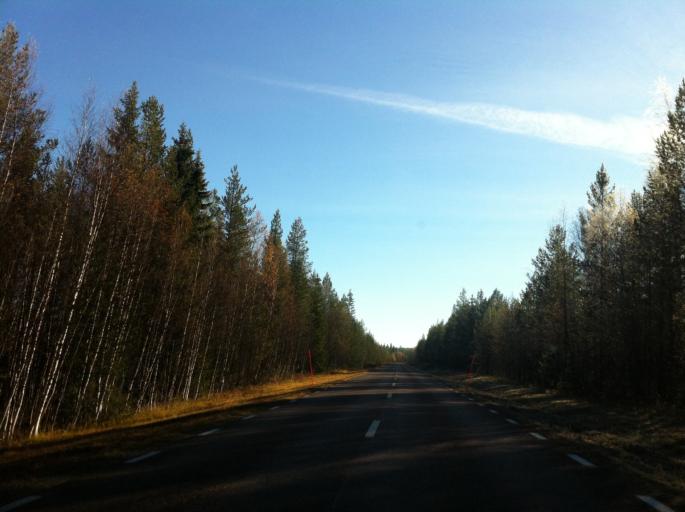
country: NO
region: Hedmark
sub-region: Trysil
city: Innbygda
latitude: 61.7086
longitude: 13.0135
